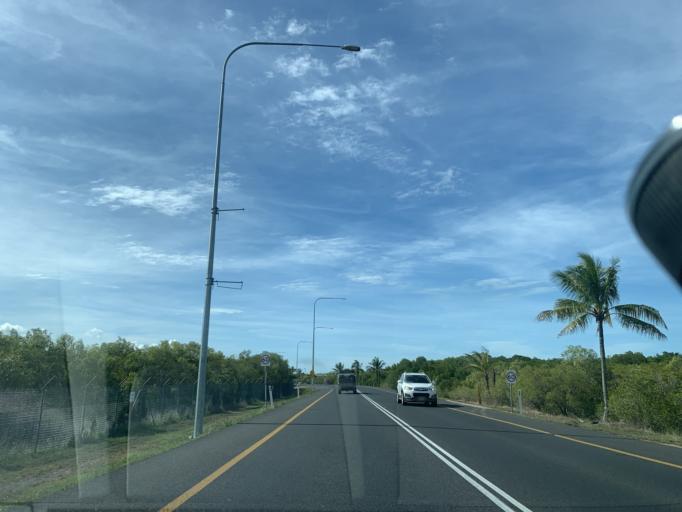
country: AU
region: Queensland
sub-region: Cairns
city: Cairns
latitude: -16.8824
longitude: 145.7604
